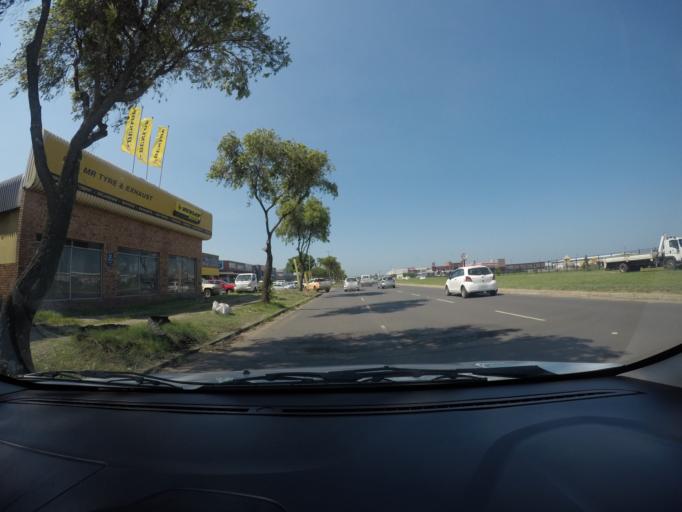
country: ZA
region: KwaZulu-Natal
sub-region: uThungulu District Municipality
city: Richards Bay
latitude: -28.7485
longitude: 32.0490
